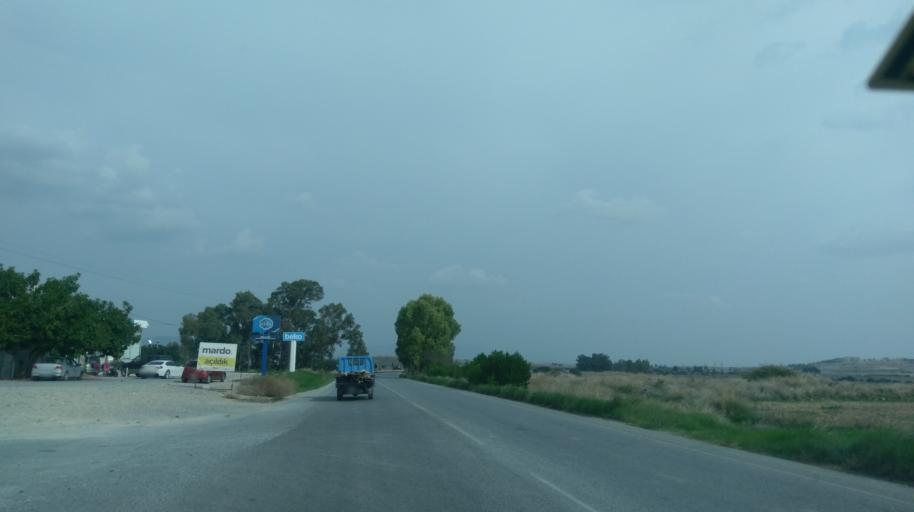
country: CY
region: Ammochostos
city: Lefkonoiko
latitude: 35.2473
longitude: 33.6113
